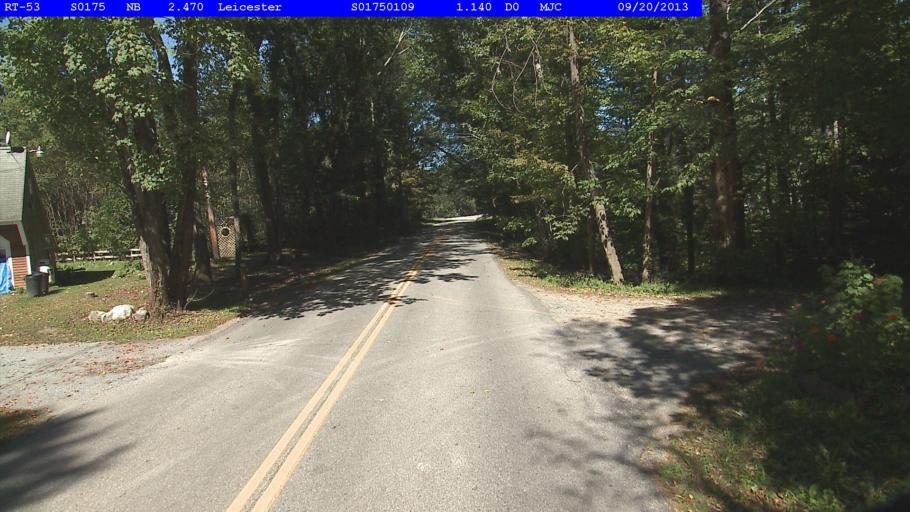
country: US
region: Vermont
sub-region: Rutland County
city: Brandon
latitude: 43.8596
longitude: -73.0679
